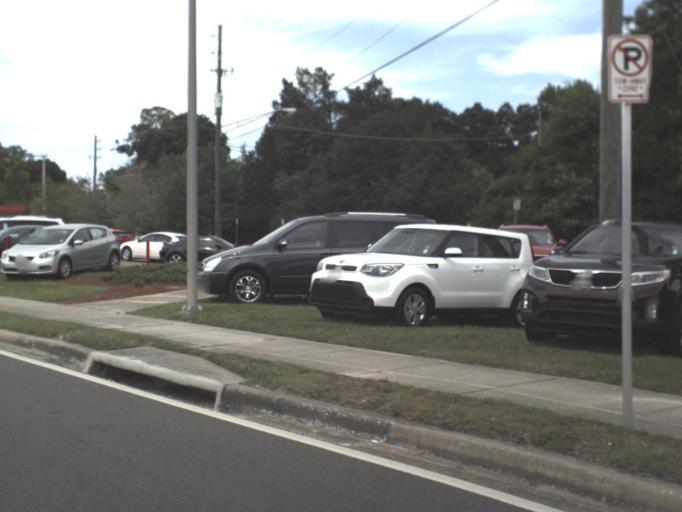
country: US
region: Florida
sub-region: Clay County
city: Bellair-Meadowbrook Terrace
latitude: 30.2346
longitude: -81.7395
